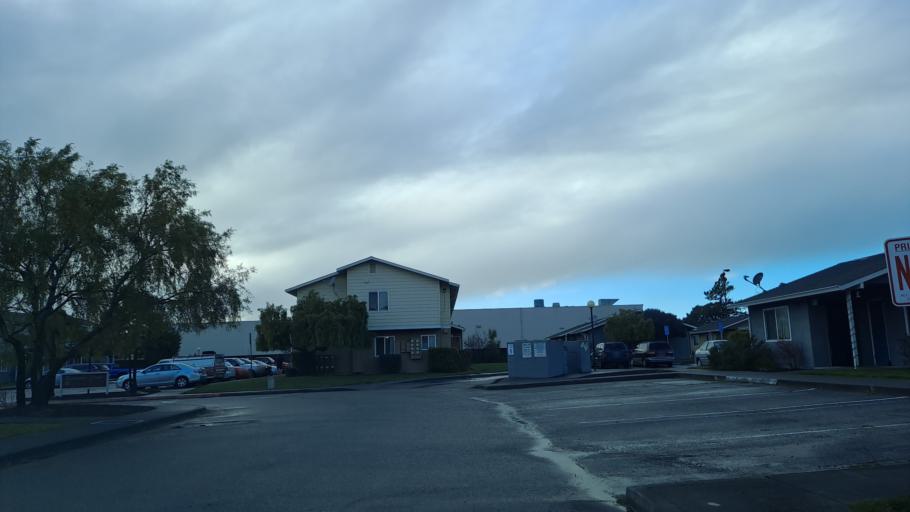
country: US
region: California
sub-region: Humboldt County
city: Fortuna
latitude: 40.5843
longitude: -124.1434
